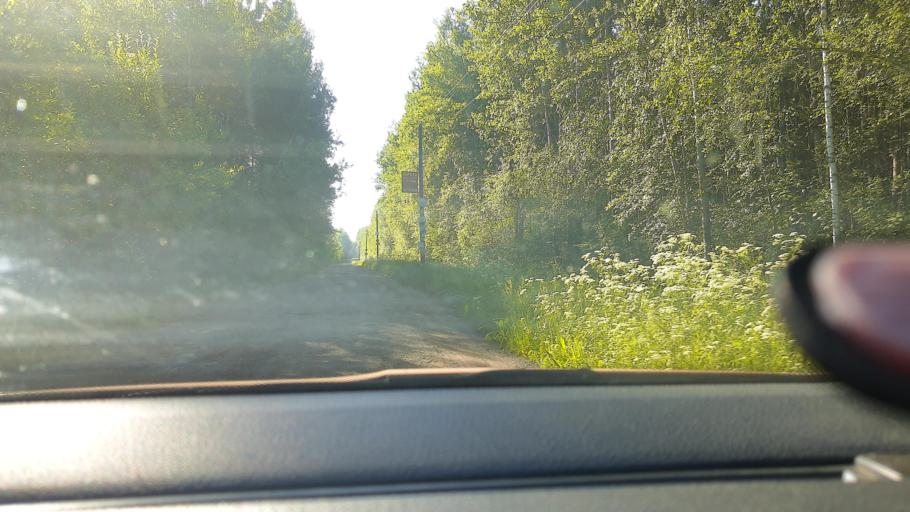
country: RU
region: Moskovskaya
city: Elektrogorsk
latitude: 55.8996
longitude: 38.7044
